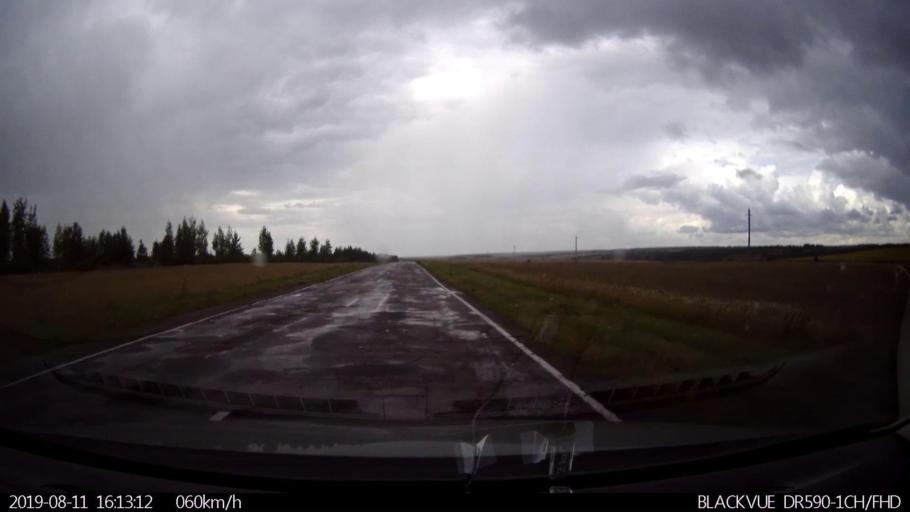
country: RU
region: Ulyanovsk
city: Ignatovka
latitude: 54.0181
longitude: 47.6378
